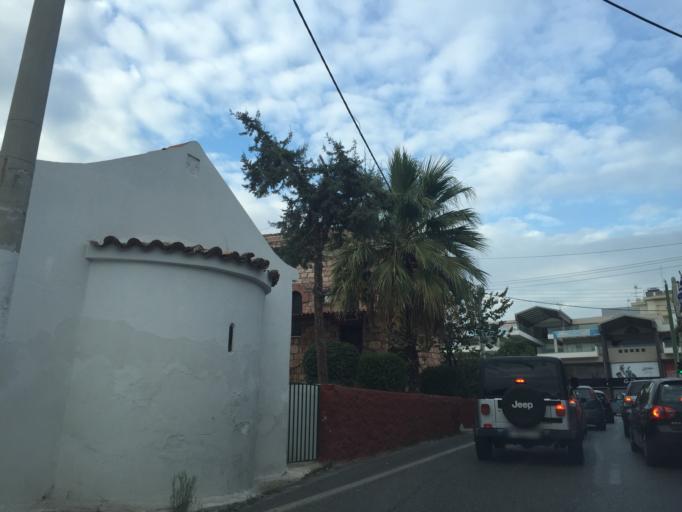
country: GR
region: Attica
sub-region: Nomarchia Anatolikis Attikis
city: Vari
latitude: 37.8329
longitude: 23.8028
